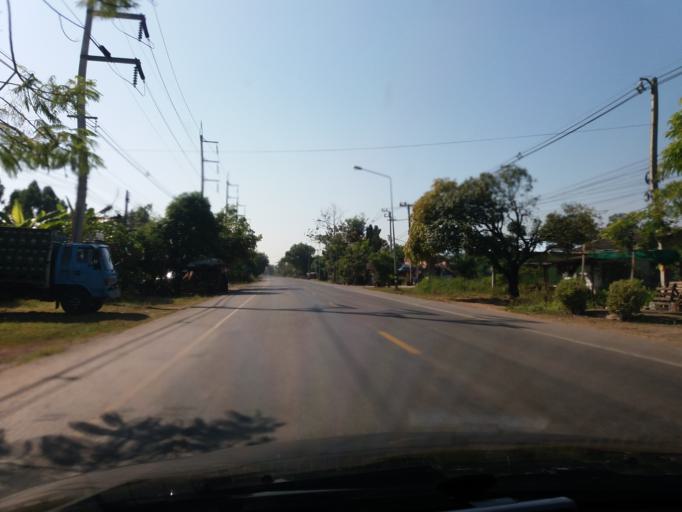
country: TH
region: Kamphaeng Phet
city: Khlong Khlung
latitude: 16.2845
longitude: 99.6994
